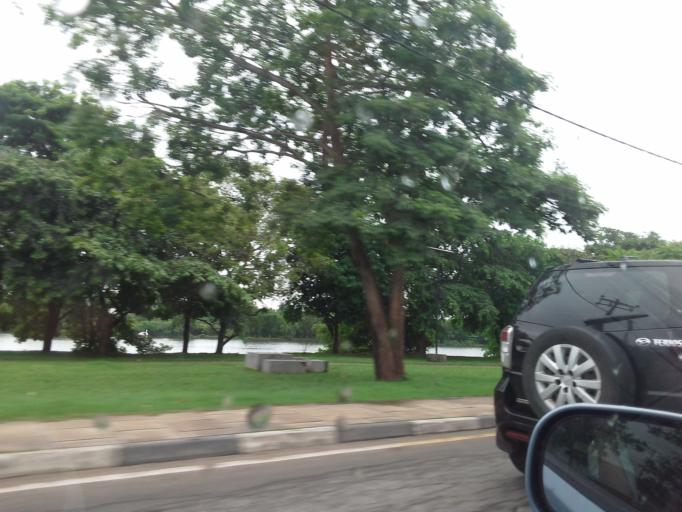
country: LK
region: Western
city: Pita Kotte
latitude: 6.9058
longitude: 79.9050
